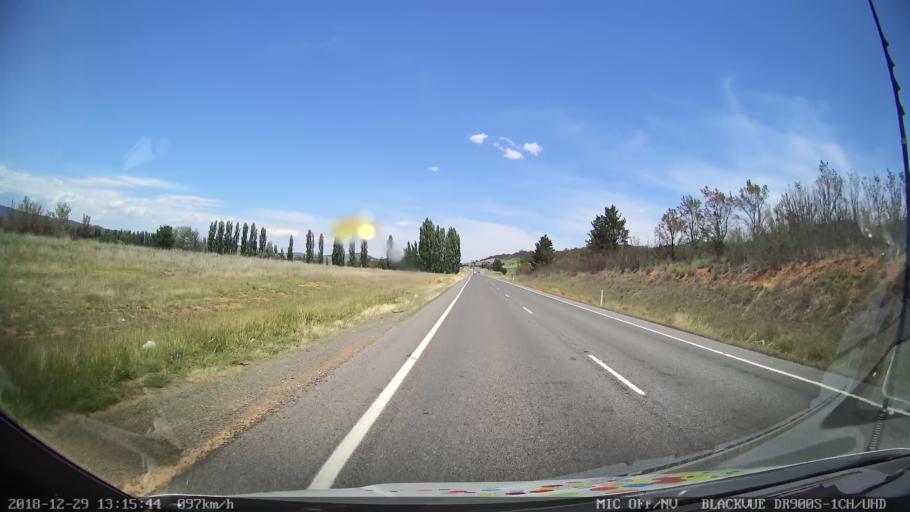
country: AU
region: Australian Capital Territory
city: Macarthur
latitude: -35.7133
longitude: 149.1587
